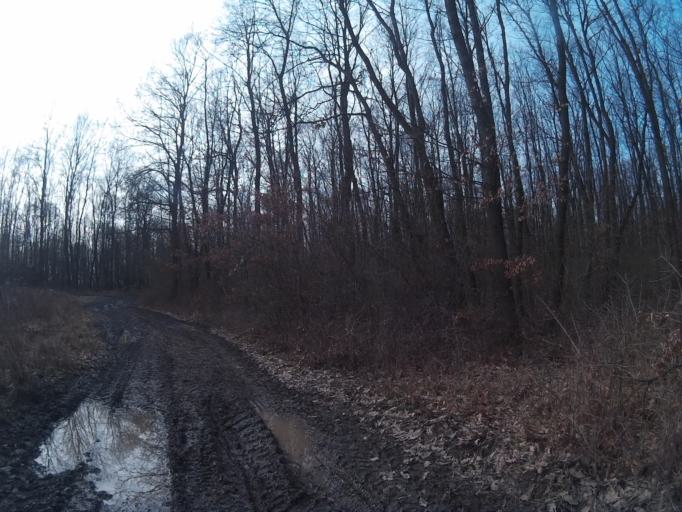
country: HU
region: Komarom-Esztergom
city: Tarjan
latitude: 47.5957
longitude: 18.4665
